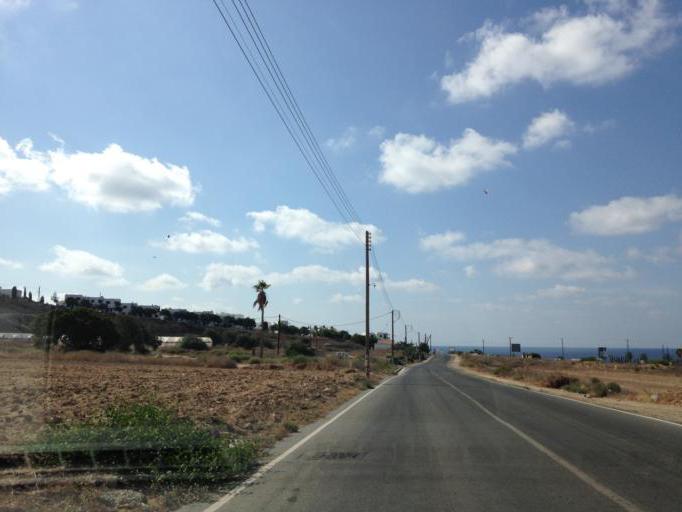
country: CY
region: Pafos
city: Chlorakas
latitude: 34.7928
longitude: 32.4038
